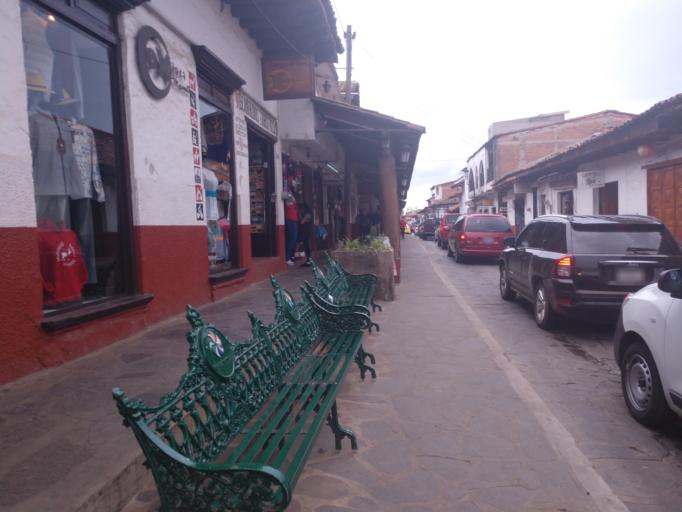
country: MX
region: Jalisco
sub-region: Mazamitla
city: Mazamitla
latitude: 19.9173
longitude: -103.0206
